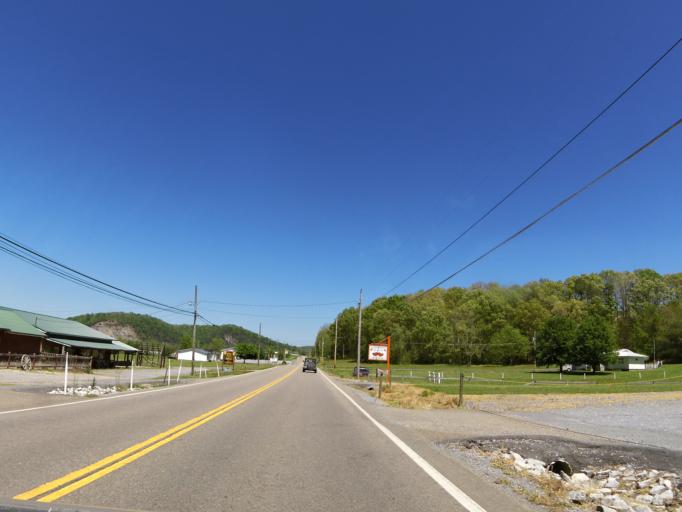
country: US
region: Tennessee
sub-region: Unicoi County
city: Erwin
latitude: 36.1977
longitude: -82.4790
